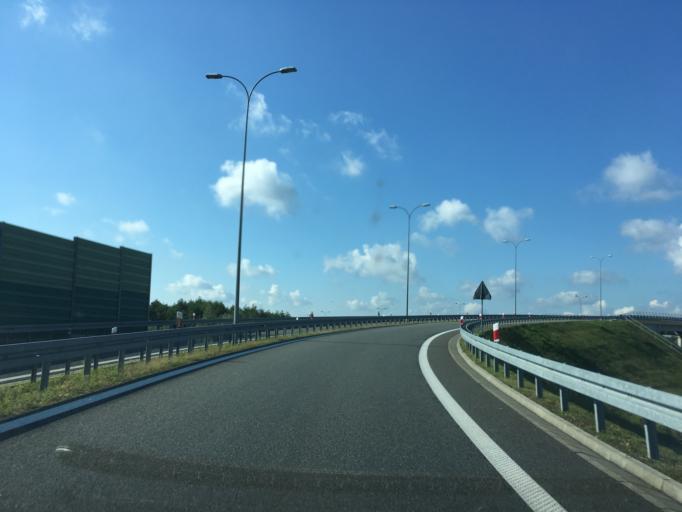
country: PL
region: Kujawsko-Pomorskie
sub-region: Powiat swiecki
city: Warlubie
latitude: 53.6050
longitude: 18.6248
